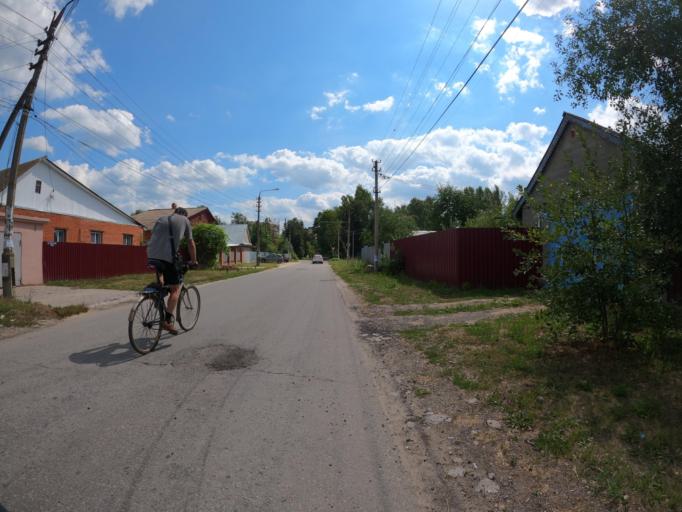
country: RU
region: Moskovskaya
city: Peski
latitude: 55.2771
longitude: 38.7465
